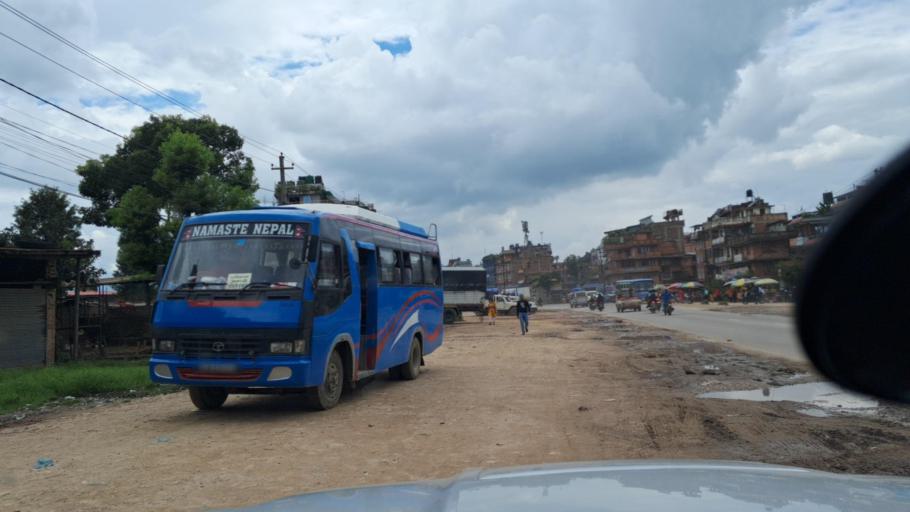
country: NP
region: Central Region
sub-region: Bagmati Zone
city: Bhaktapur
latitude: 27.6660
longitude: 85.4386
